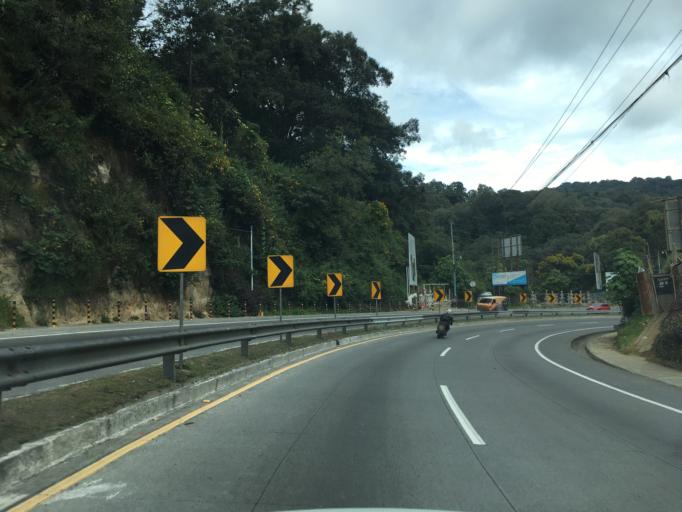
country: GT
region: Sacatepequez
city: San Lucas Sacatepequez
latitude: 14.6123
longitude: -90.6515
